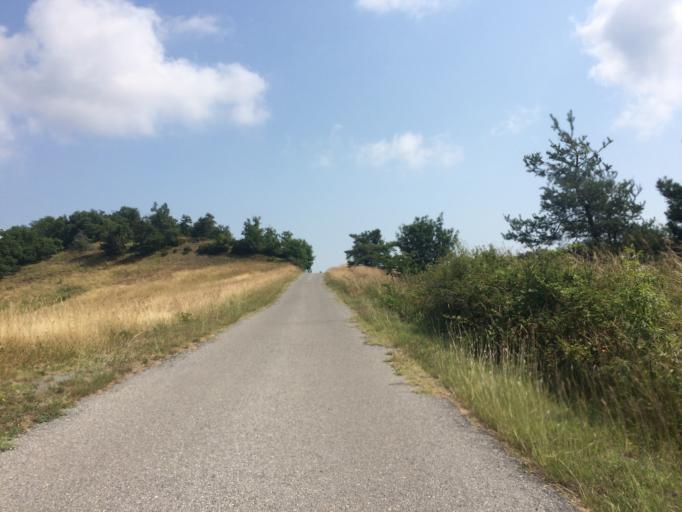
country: IT
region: Piedmont
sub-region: Provincia di Alessandria
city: Pareto
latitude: 44.4994
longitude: 8.3673
